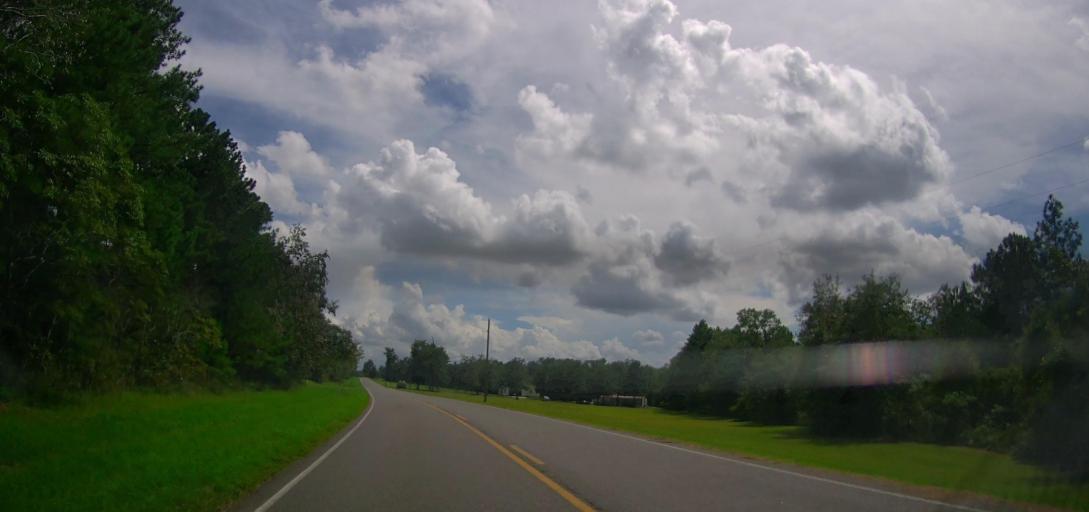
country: US
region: Georgia
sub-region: Taylor County
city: Butler
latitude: 32.4784
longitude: -84.2056
